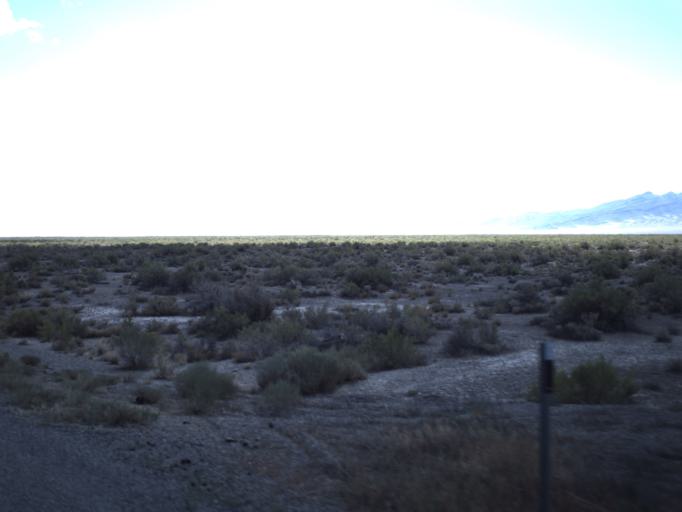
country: US
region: Nevada
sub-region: White Pine County
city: McGill
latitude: 39.0519
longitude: -113.9801
